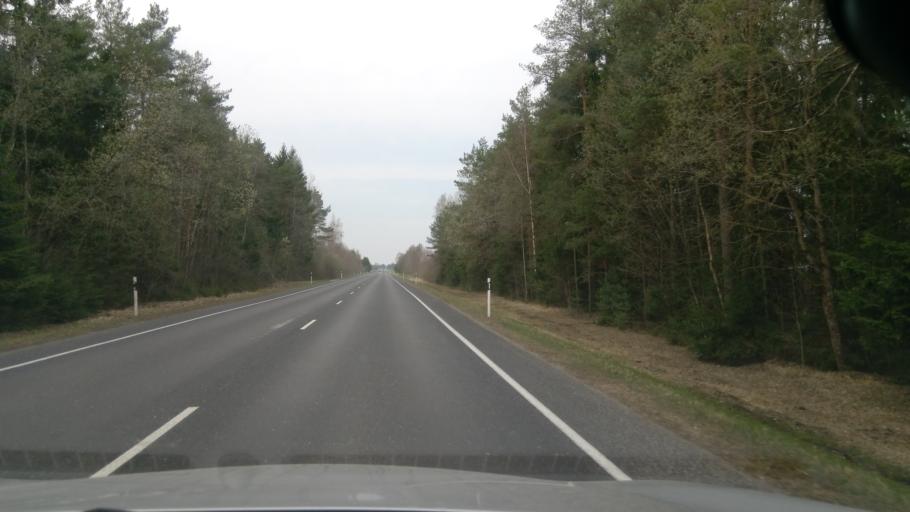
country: EE
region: Viljandimaa
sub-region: Vohma linn
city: Vohma
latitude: 58.7406
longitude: 25.5825
